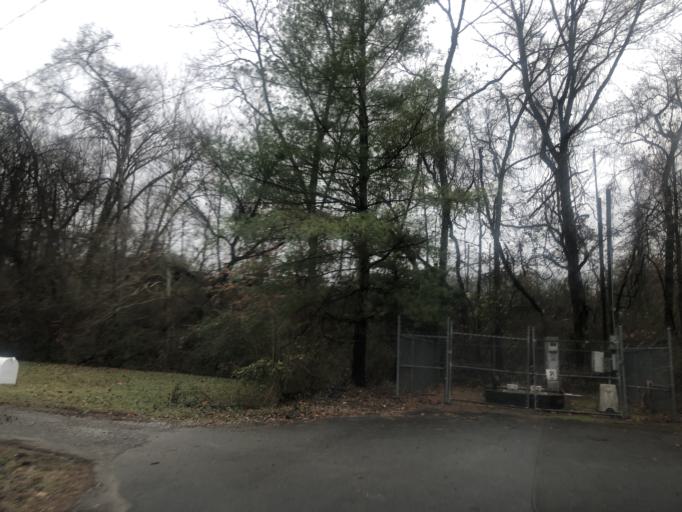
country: US
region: Tennessee
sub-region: Davidson County
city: Lakewood
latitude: 36.1426
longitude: -86.6718
